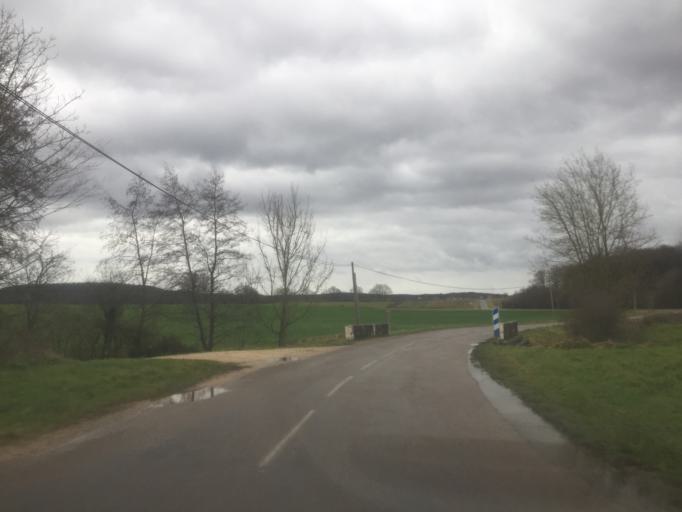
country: FR
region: Franche-Comte
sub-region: Departement de la Haute-Saone
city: Pesmes
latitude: 47.2222
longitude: 5.5025
